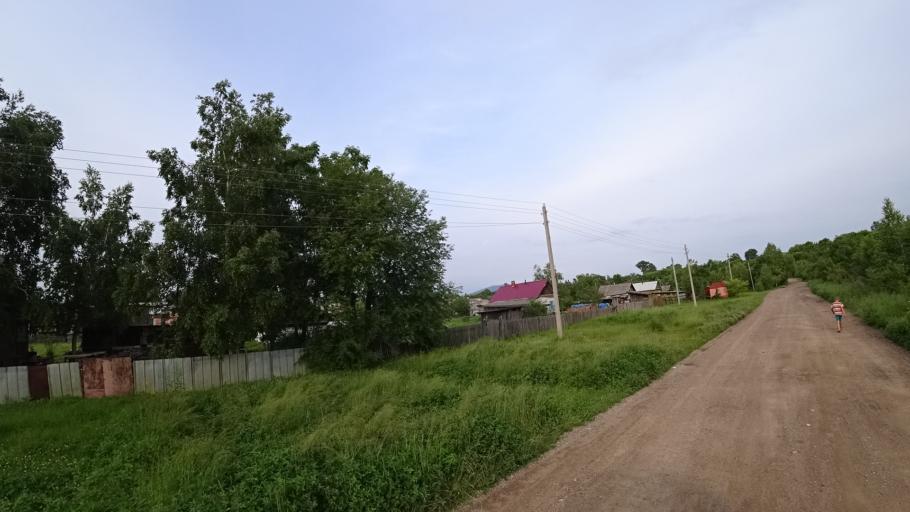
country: RU
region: Primorskiy
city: Novosysoyevka
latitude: 44.2440
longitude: 133.3606
